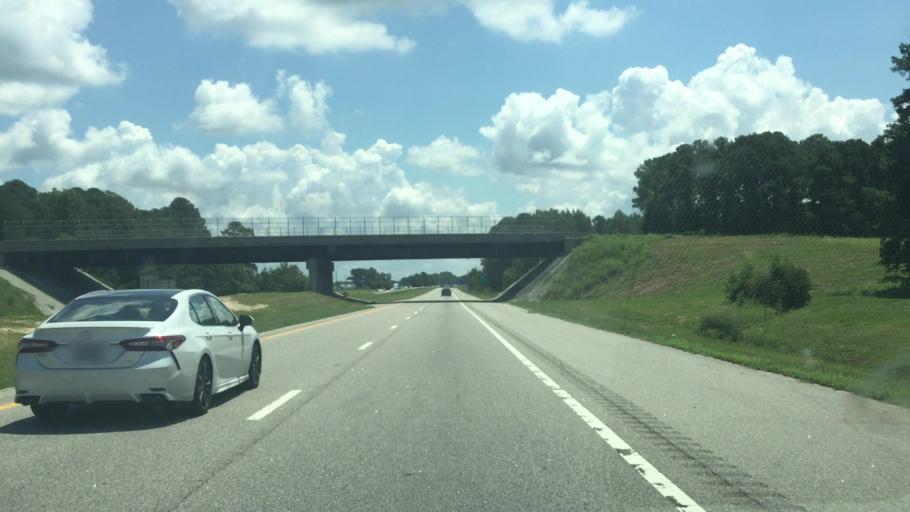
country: US
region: North Carolina
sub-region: Robeson County
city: Lumberton
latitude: 34.5905
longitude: -79.0698
